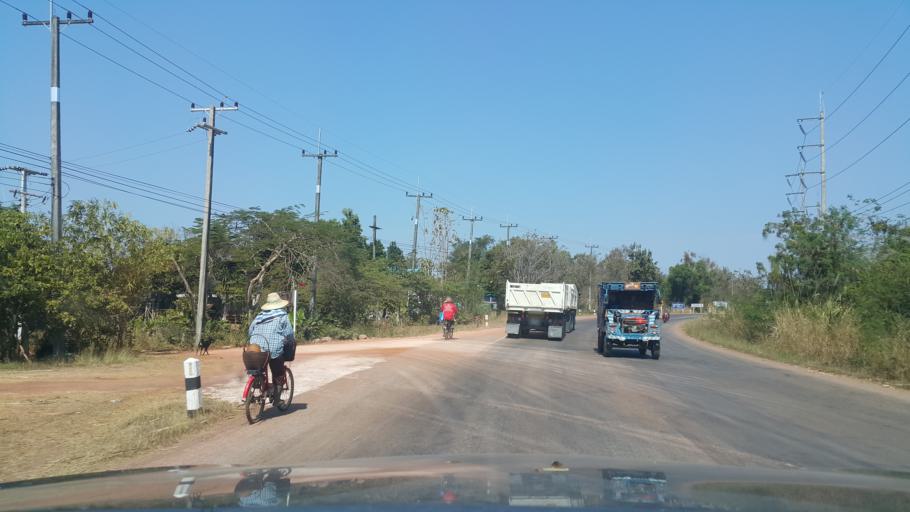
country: TH
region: Changwat Udon Thani
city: Ban Dung
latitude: 17.6050
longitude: 103.2456
